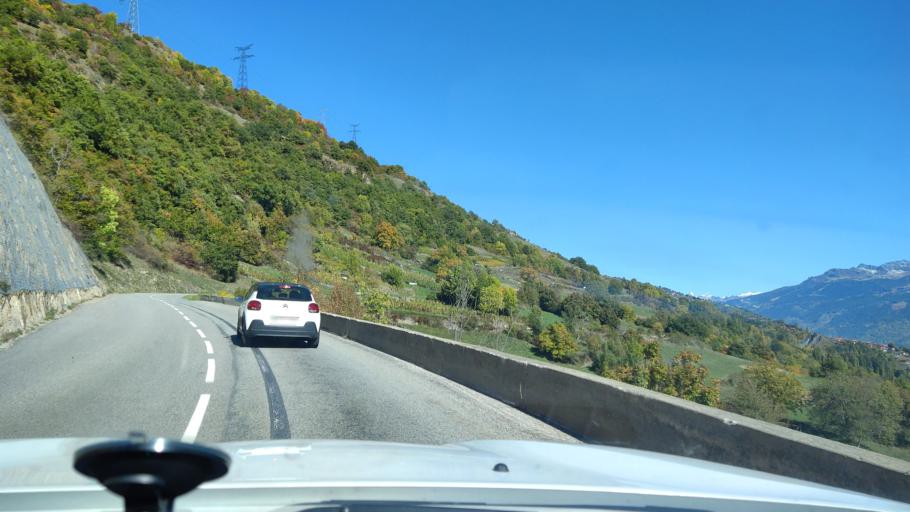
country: FR
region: Rhone-Alpes
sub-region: Departement de la Savoie
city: Aime
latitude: 45.5582
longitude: 6.6354
